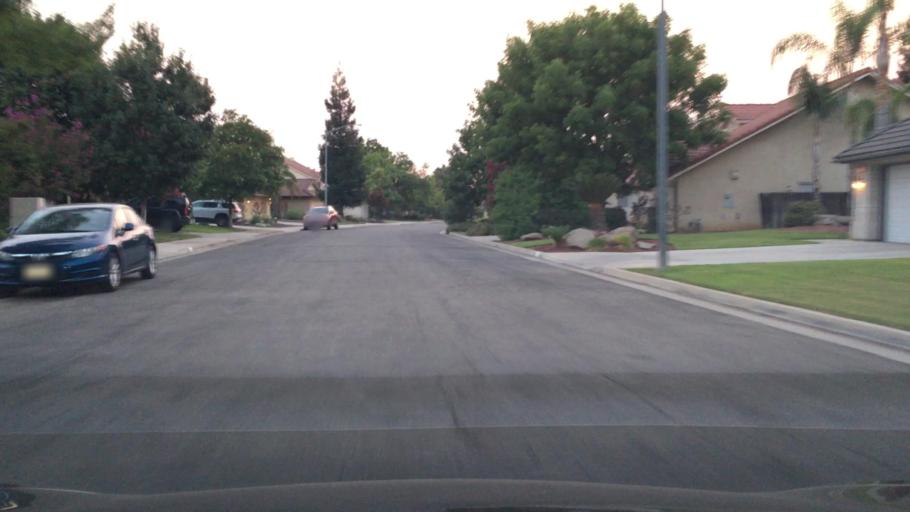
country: US
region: California
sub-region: Fresno County
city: Clovis
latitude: 36.8714
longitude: -119.7446
